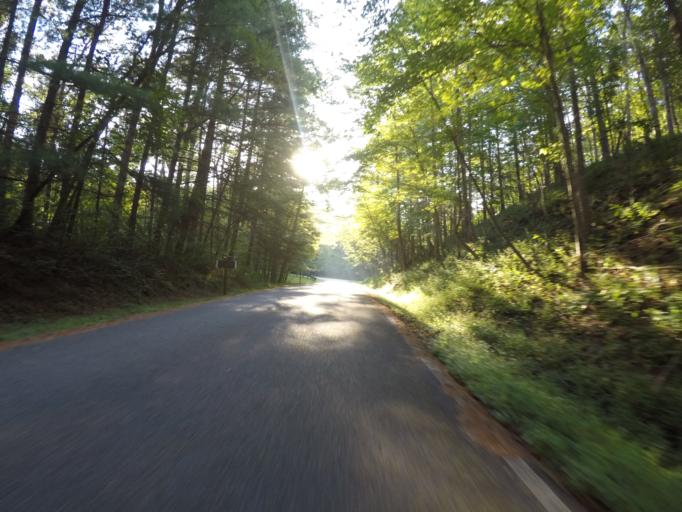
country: US
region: Ohio
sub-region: Lawrence County
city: Ironton
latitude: 38.6108
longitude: -82.6162
